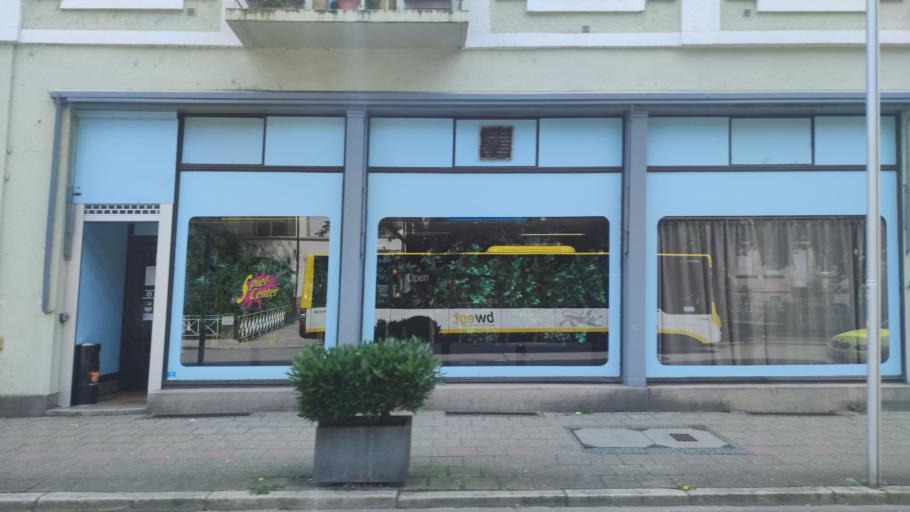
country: DE
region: Baden-Wuerttemberg
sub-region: Karlsruhe Region
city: Baden-Baden
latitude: 48.7660
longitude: 8.2351
